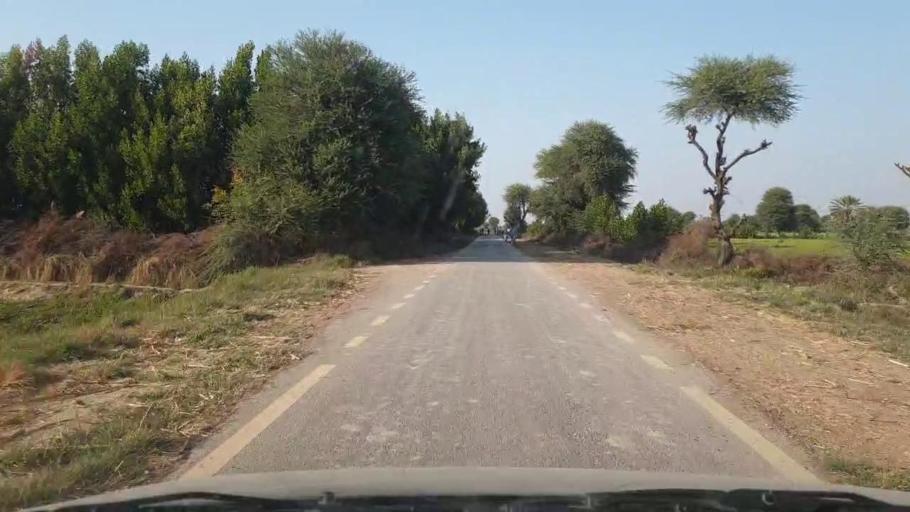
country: PK
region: Sindh
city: Samaro
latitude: 25.2982
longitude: 69.3485
